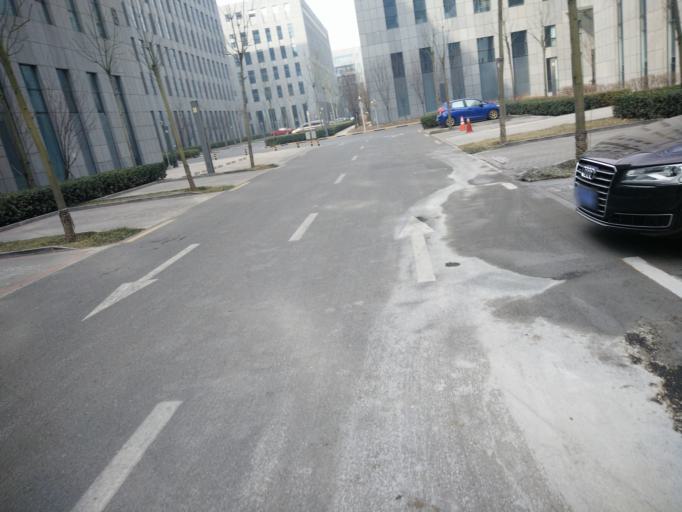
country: CN
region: Beijing
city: Jiugong
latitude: 39.7598
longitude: 116.5099
